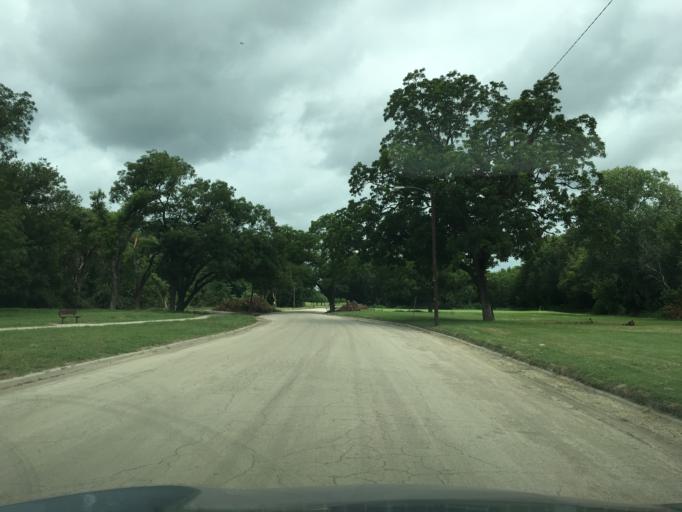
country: US
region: Texas
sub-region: Dallas County
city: University Park
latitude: 32.8778
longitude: -96.7450
